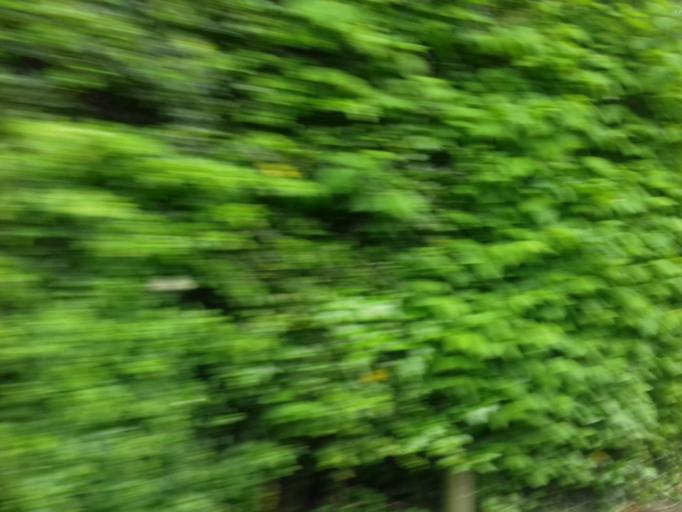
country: IE
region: Leinster
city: Donabate
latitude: 53.4869
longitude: -6.1698
